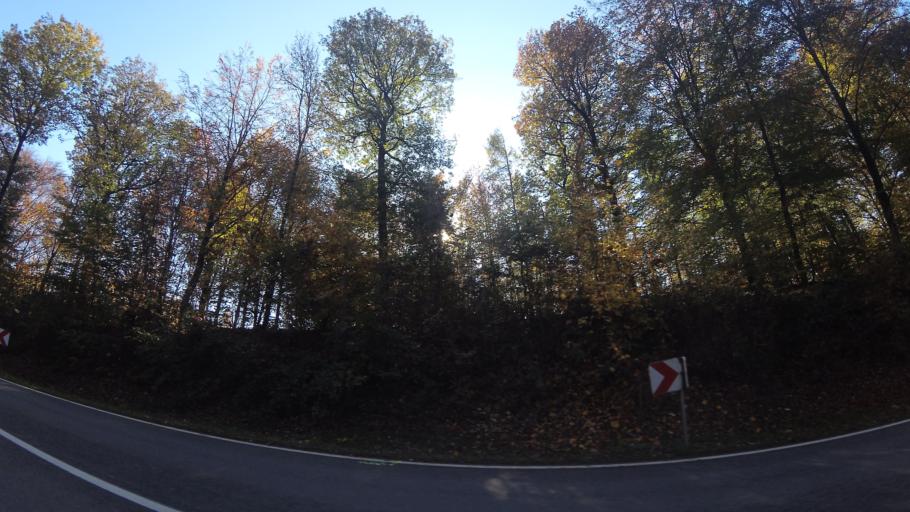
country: DE
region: Saarland
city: Weiskirchen
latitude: 49.5409
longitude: 6.8400
